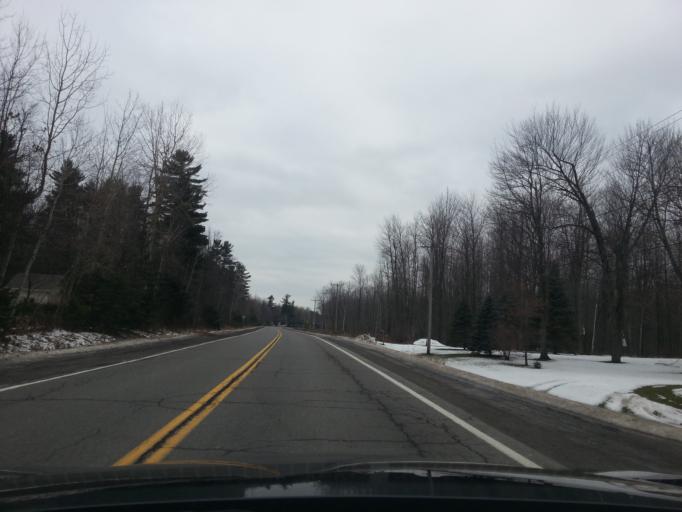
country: CA
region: Ontario
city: Clarence-Rockland
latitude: 45.4235
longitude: -75.4406
